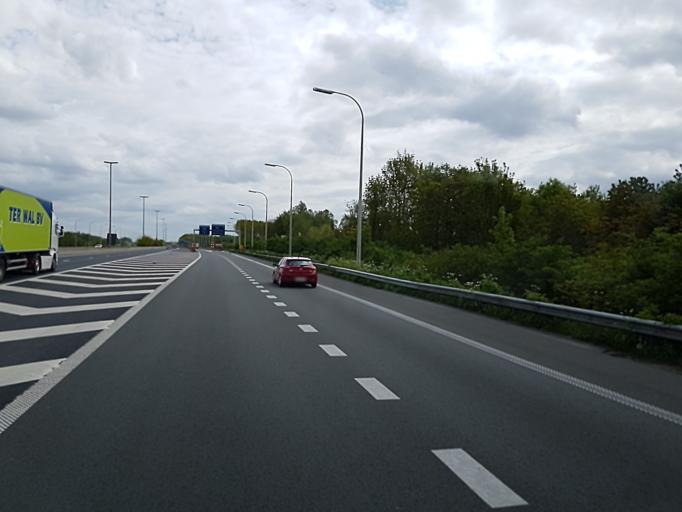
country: BE
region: Wallonia
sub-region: Province du Hainaut
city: Mouscron
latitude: 50.7941
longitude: 3.2222
